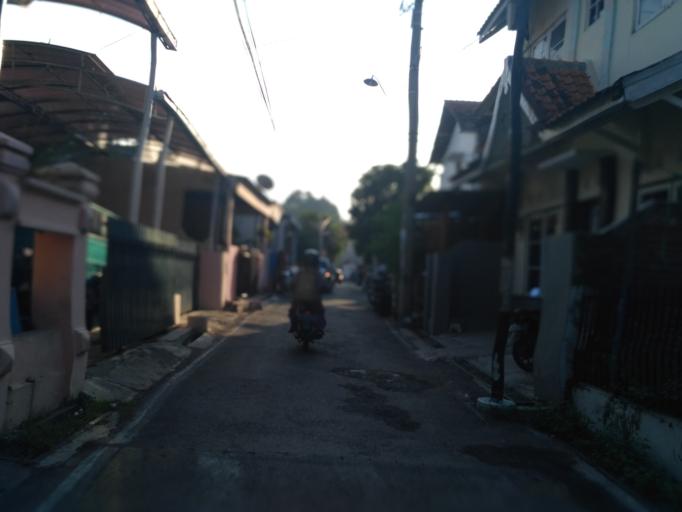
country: ID
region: Central Java
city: Semarang
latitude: -6.9885
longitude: 110.4157
